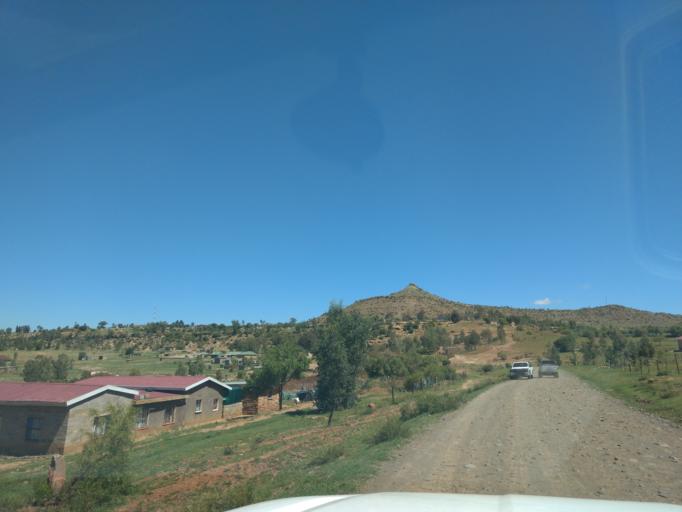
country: LS
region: Maseru
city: Maseru
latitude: -29.4890
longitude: 27.3710
